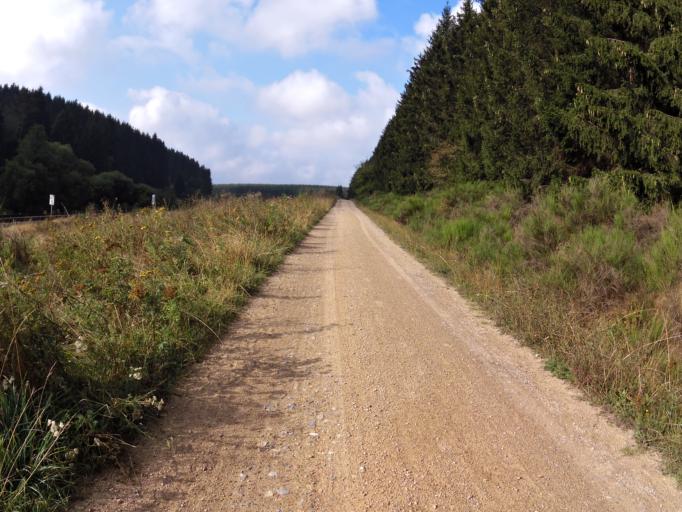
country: DE
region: North Rhine-Westphalia
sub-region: Regierungsbezirk Koln
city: Nettersheim
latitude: 50.4531
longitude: 6.6071
